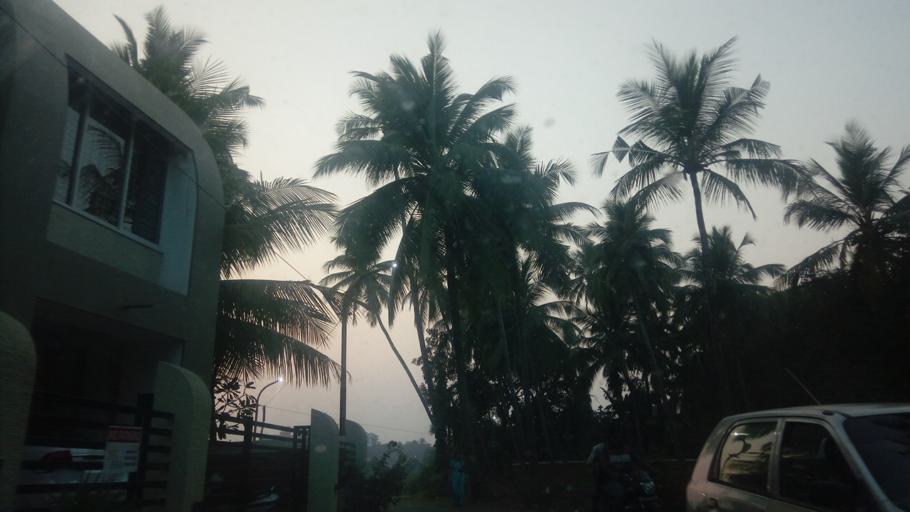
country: IN
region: Goa
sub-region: South Goa
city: Madgaon
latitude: 15.2886
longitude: 73.9593
